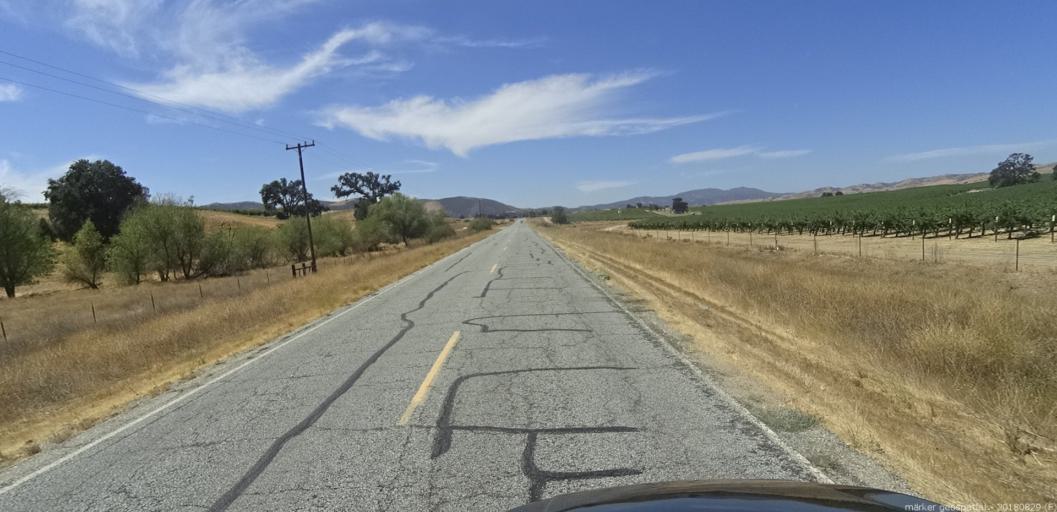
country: US
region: California
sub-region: San Luis Obispo County
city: Lake Nacimiento
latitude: 35.8724
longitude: -120.8727
